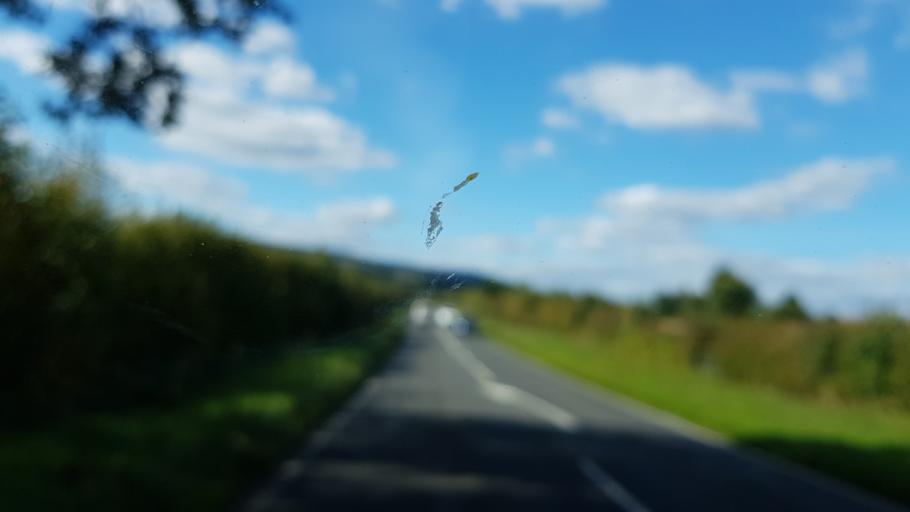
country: GB
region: England
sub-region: West Sussex
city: Petworth
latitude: 51.0378
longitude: -0.6388
